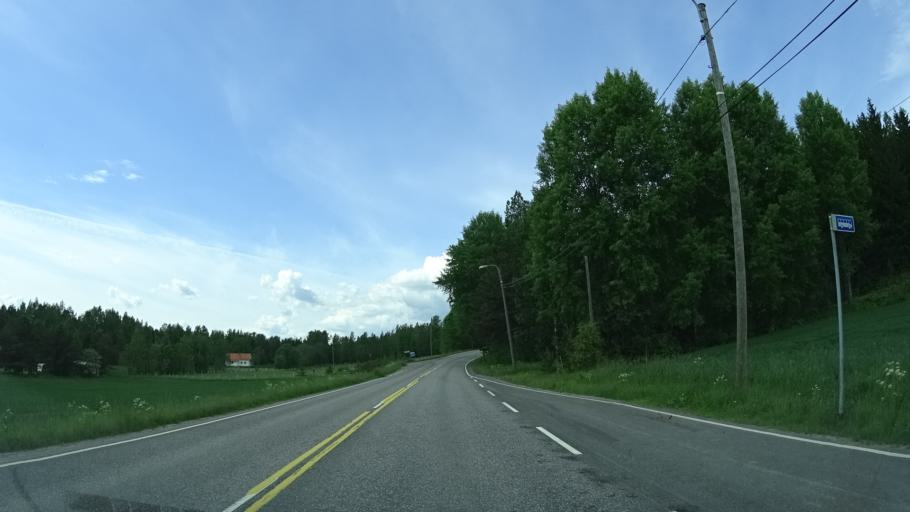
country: FI
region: Uusimaa
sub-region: Helsinki
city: Kirkkonummi
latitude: 60.2055
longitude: 24.4964
